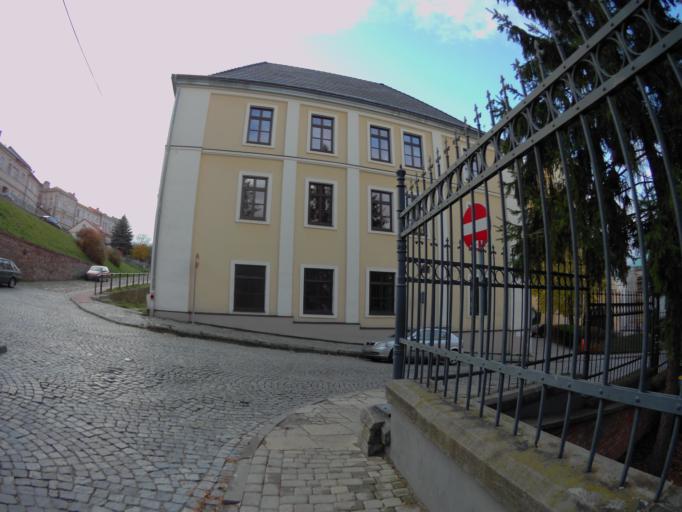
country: PL
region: Subcarpathian Voivodeship
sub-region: Przemysl
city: Przemysl
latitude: 49.7806
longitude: 22.7713
